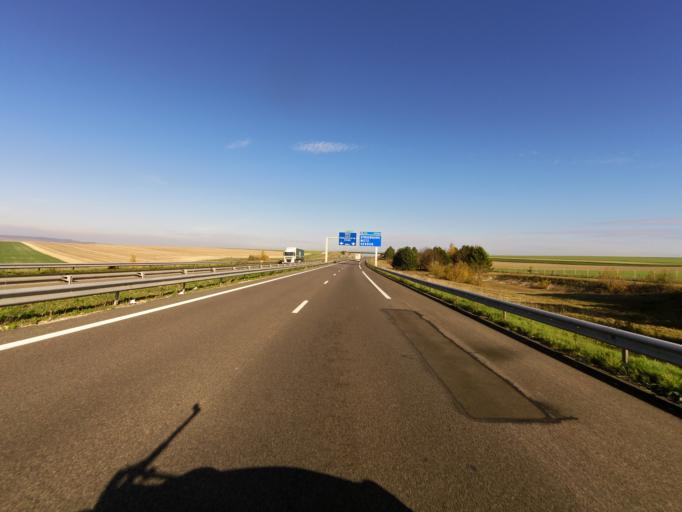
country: FR
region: Champagne-Ardenne
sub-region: Departement de la Marne
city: Fagnieres
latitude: 49.0424
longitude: 4.2814
